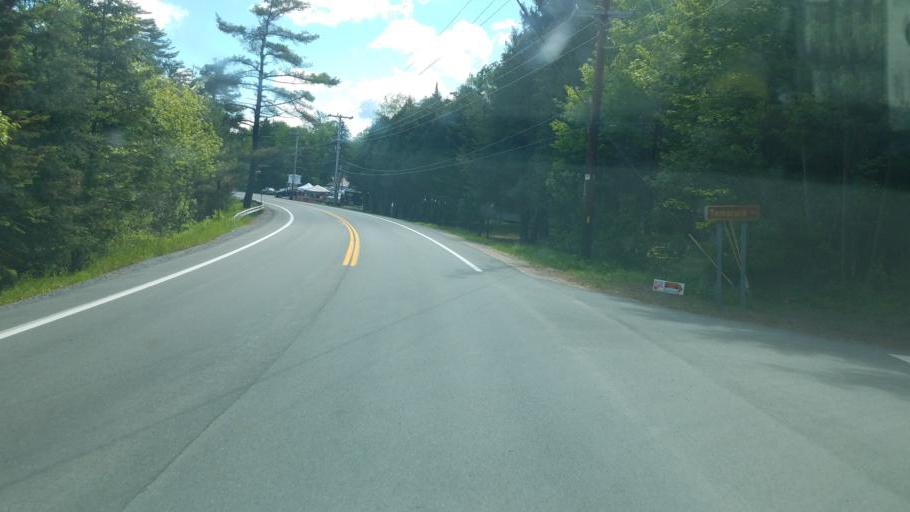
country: US
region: New York
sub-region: Oneida County
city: Boonville
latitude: 43.5355
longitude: -75.1470
